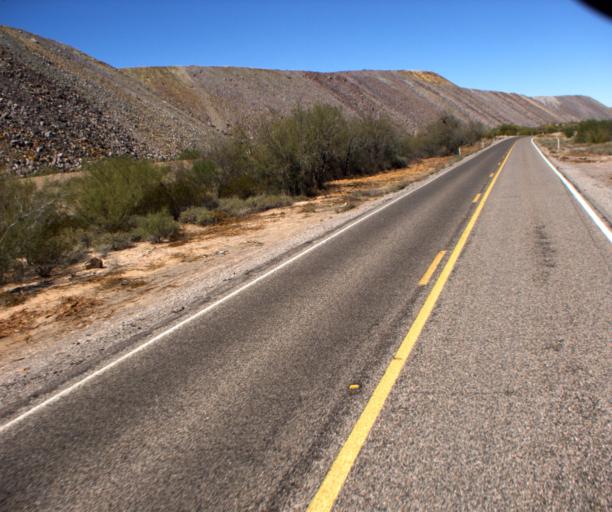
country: US
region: Arizona
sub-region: Pima County
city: Ajo
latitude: 32.3568
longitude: -112.8284
